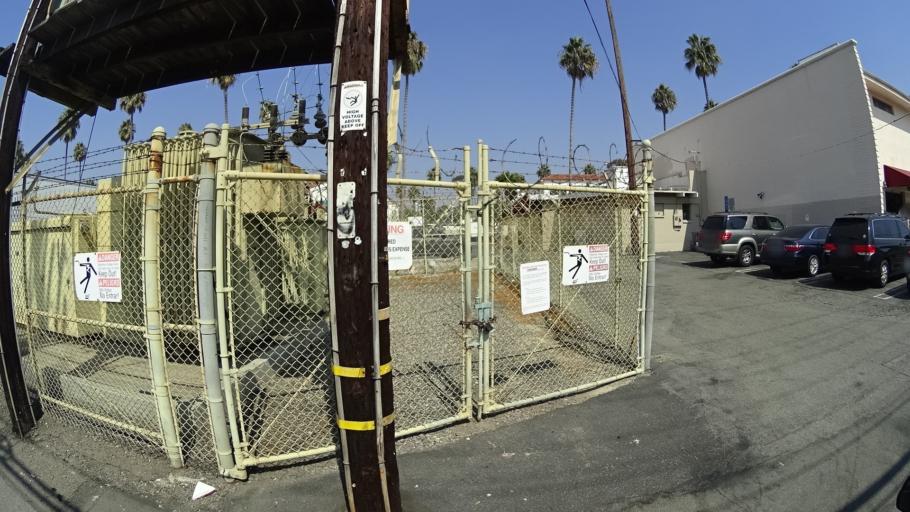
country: US
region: California
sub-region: Orange County
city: San Clemente
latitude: 33.4295
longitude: -117.6162
